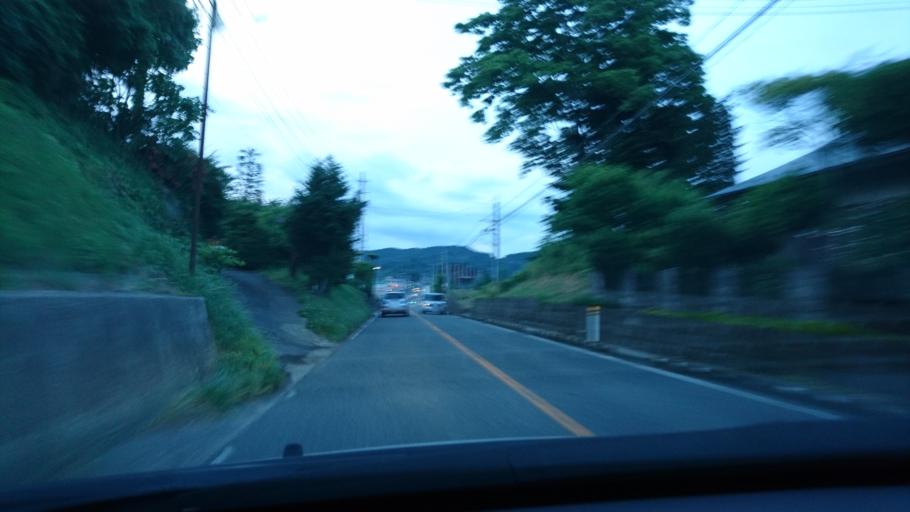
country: JP
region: Iwate
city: Ichinoseki
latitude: 38.8211
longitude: 140.9856
